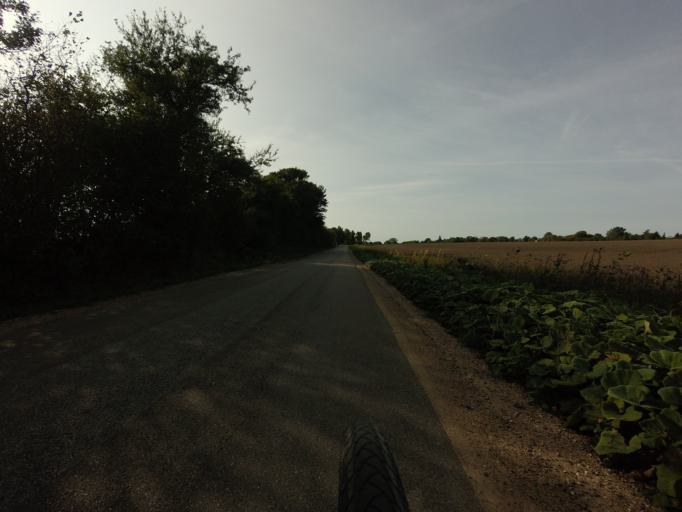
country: DK
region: Zealand
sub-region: Faxe Kommune
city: Fakse
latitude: 55.1917
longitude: 12.1107
